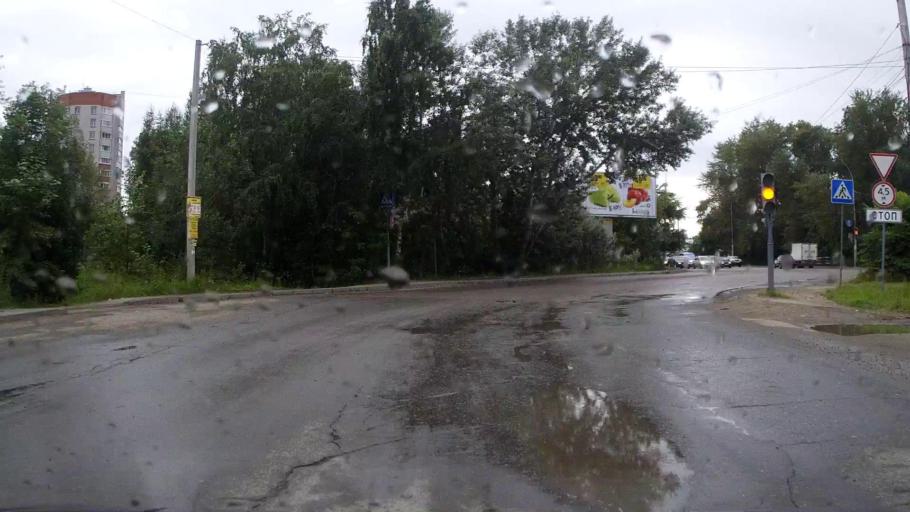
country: RU
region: Vologda
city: Vologda
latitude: 59.2053
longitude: 39.8741
